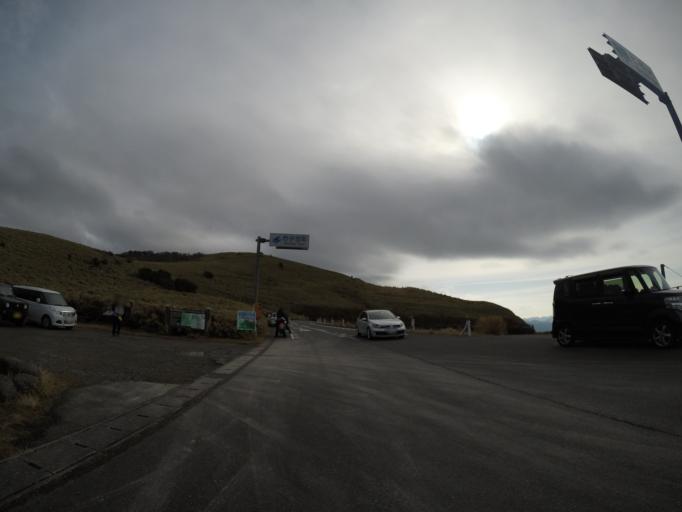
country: JP
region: Shizuoka
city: Heda
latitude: 34.8629
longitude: 138.8436
